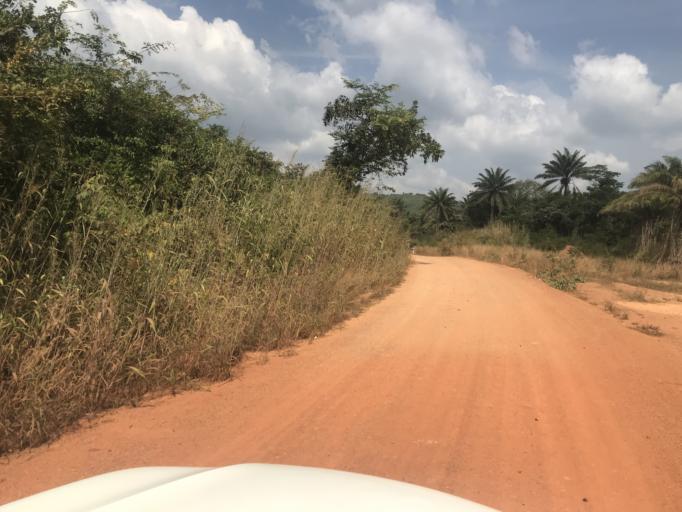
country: NG
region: Osun
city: Inisa
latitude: 7.8913
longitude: 4.3970
